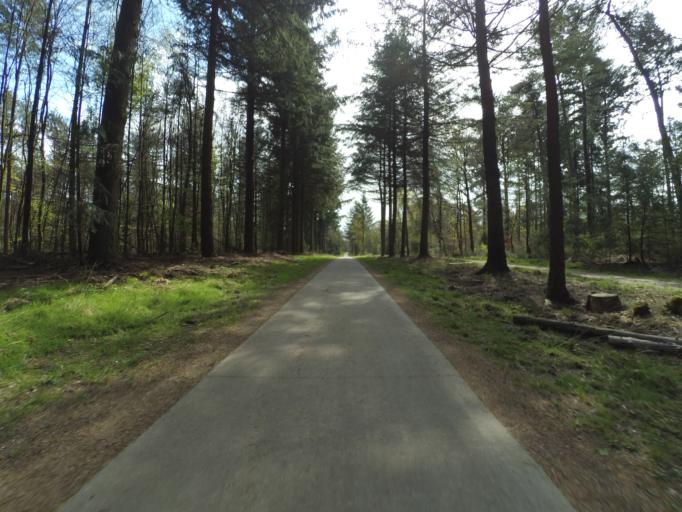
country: NL
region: Gelderland
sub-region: Gemeente Epe
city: Epe
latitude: 52.3809
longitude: 5.9300
